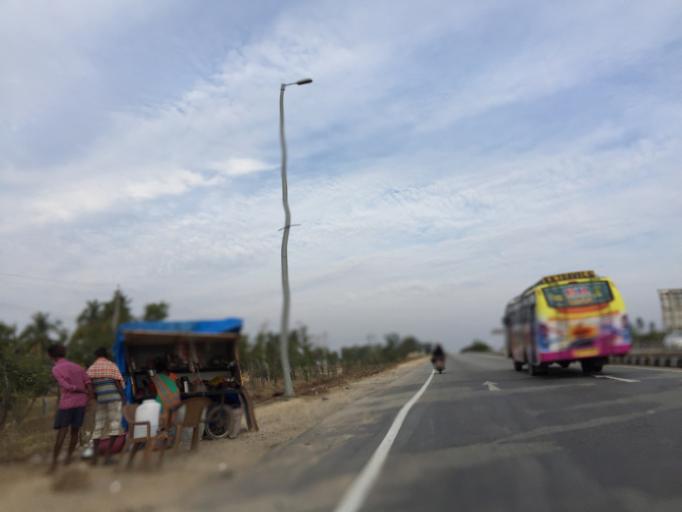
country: IN
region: Karnataka
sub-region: Kolar
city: Mulbagal
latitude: 13.1490
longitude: 78.2931
